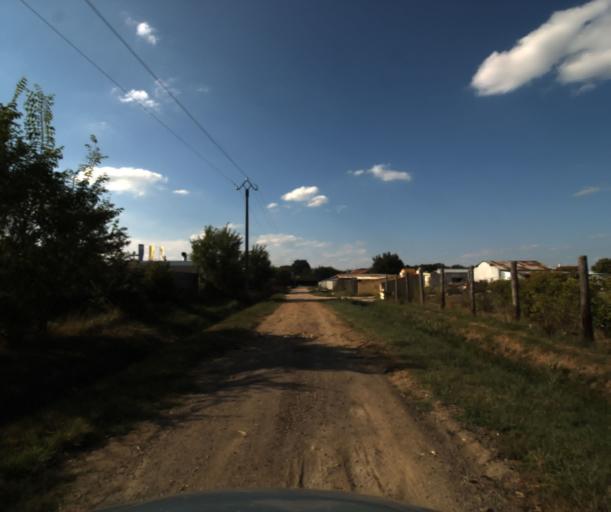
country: FR
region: Midi-Pyrenees
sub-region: Departement de la Haute-Garonne
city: Saint-Lys
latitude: 43.5127
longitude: 1.2007
